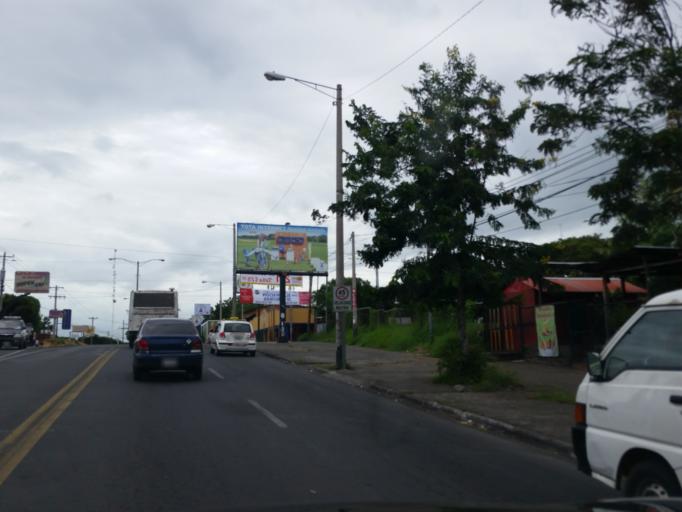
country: NI
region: Managua
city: Managua
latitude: 12.1453
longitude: -86.2295
